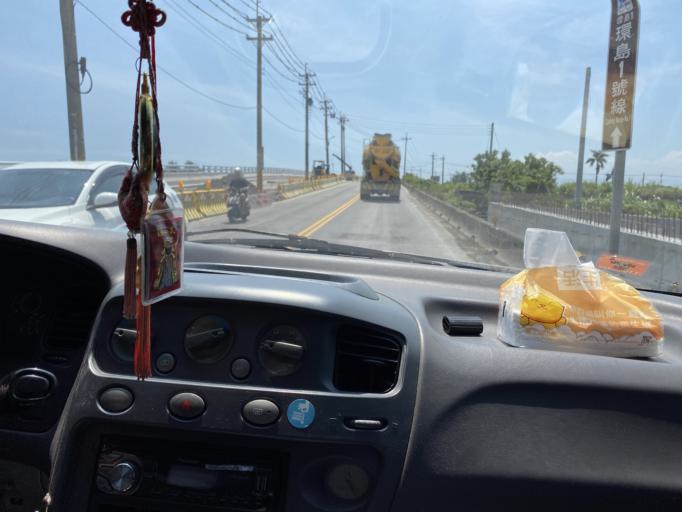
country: TW
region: Taiwan
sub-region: Yilan
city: Yilan
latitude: 24.8465
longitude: 121.8230
